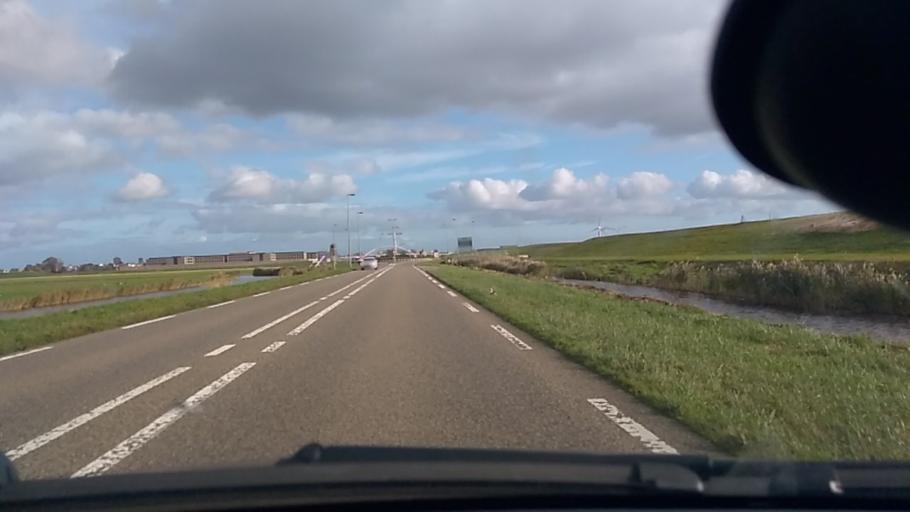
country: NL
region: North Holland
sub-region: Gemeente Zaanstad
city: Zaanstad
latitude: 52.4336
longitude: 4.7578
